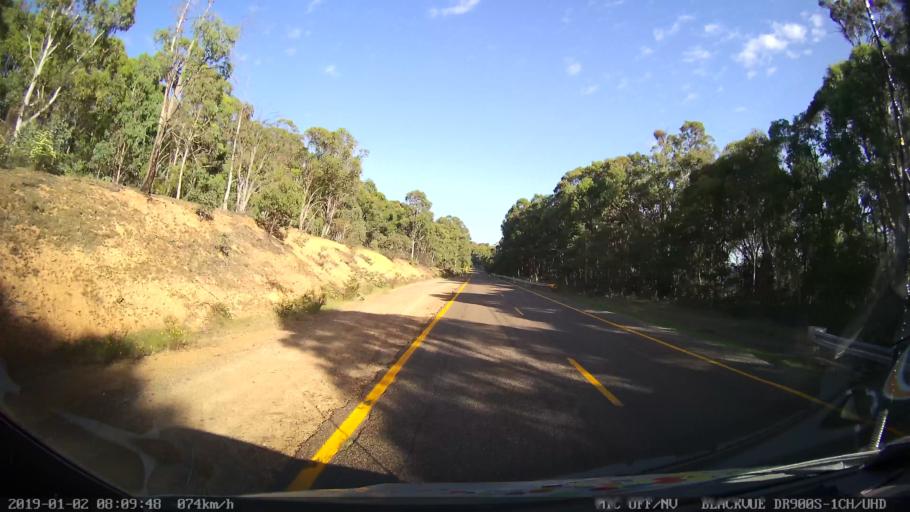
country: AU
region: New South Wales
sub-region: Tumut Shire
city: Tumut
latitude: -35.6037
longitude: 148.3763
